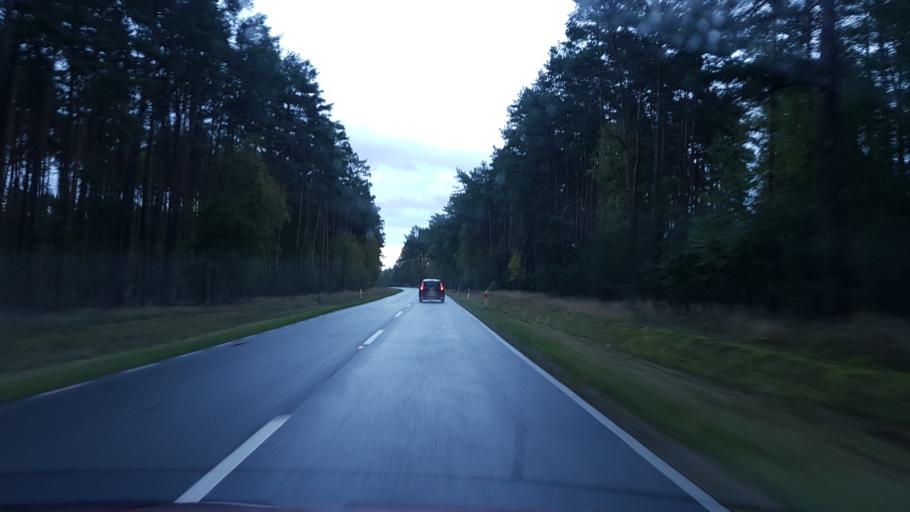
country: PL
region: Greater Poland Voivodeship
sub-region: Powiat pilski
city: Pila
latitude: 53.1928
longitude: 16.8214
